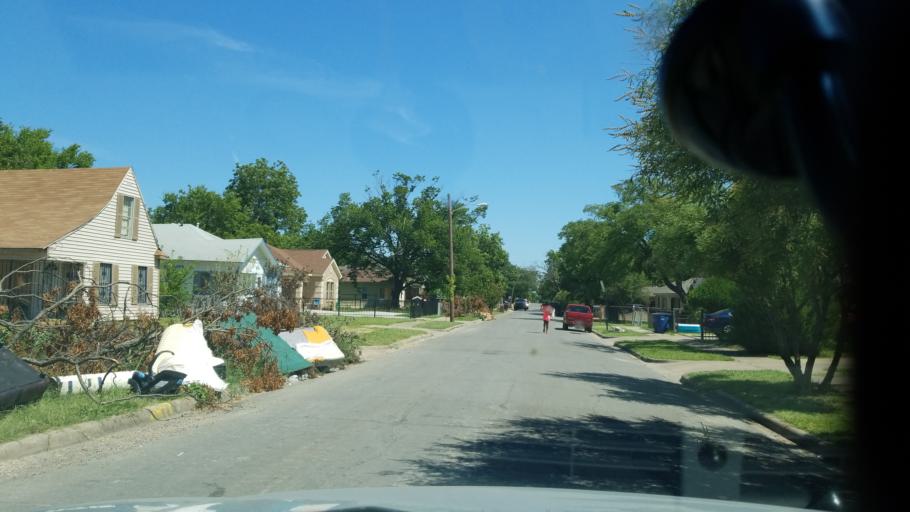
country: US
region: Texas
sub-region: Dallas County
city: Cockrell Hill
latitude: 32.7114
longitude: -96.8194
